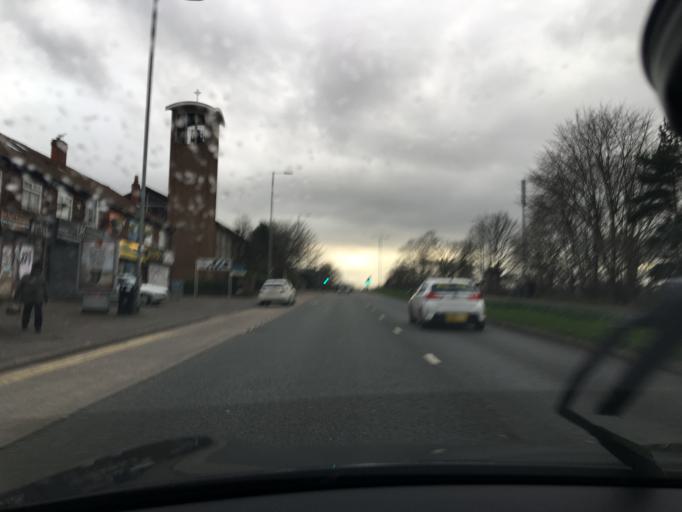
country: GB
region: England
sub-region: Manchester
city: Chorlton cum Hardy
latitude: 53.4334
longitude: -2.2477
